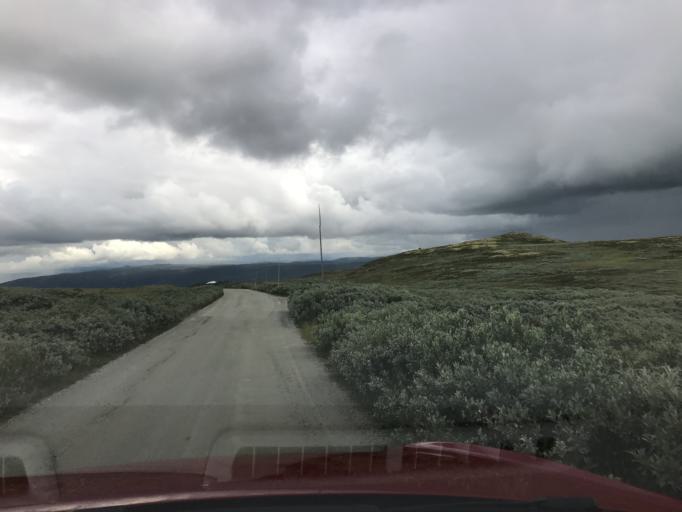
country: NO
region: Buskerud
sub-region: Hol
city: Geilo
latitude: 60.5456
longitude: 8.1205
